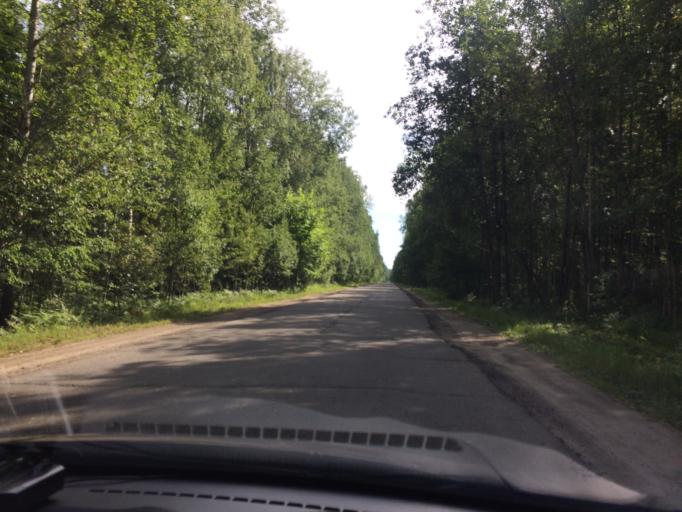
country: RU
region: Mariy-El
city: Surok
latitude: 56.5712
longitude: 48.1841
